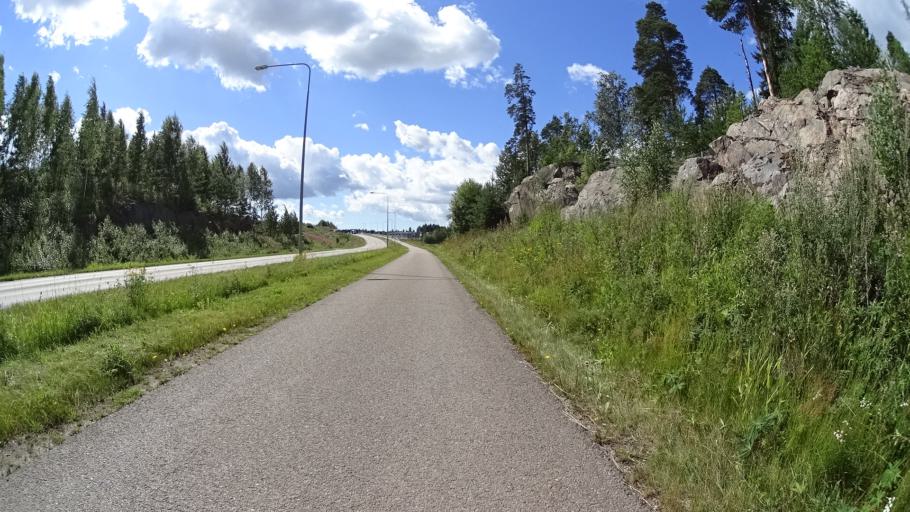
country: FI
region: Uusimaa
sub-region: Helsinki
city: Teekkarikylae
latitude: 60.3140
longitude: 24.8955
